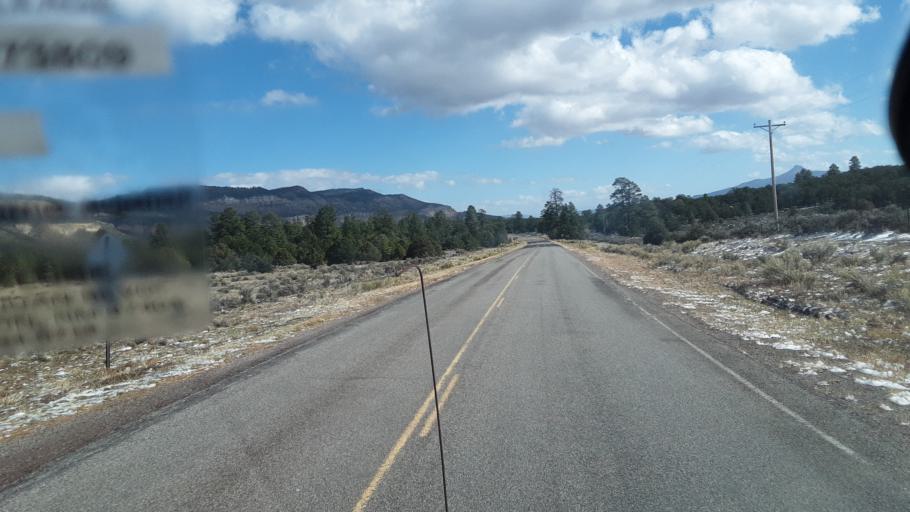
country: US
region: New Mexico
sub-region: Rio Arriba County
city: Santa Teresa
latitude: 36.2008
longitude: -106.7346
